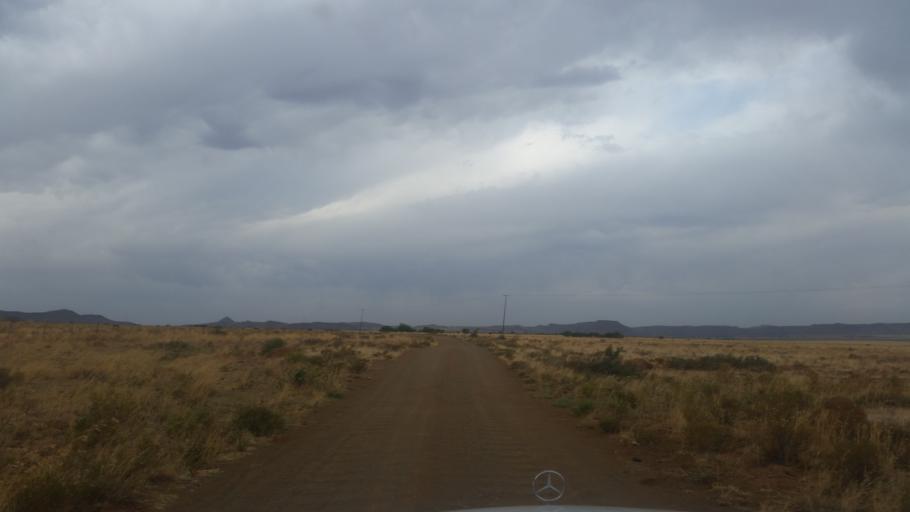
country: ZA
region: Orange Free State
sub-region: Xhariep District Municipality
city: Trompsburg
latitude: -30.5068
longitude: 25.9380
